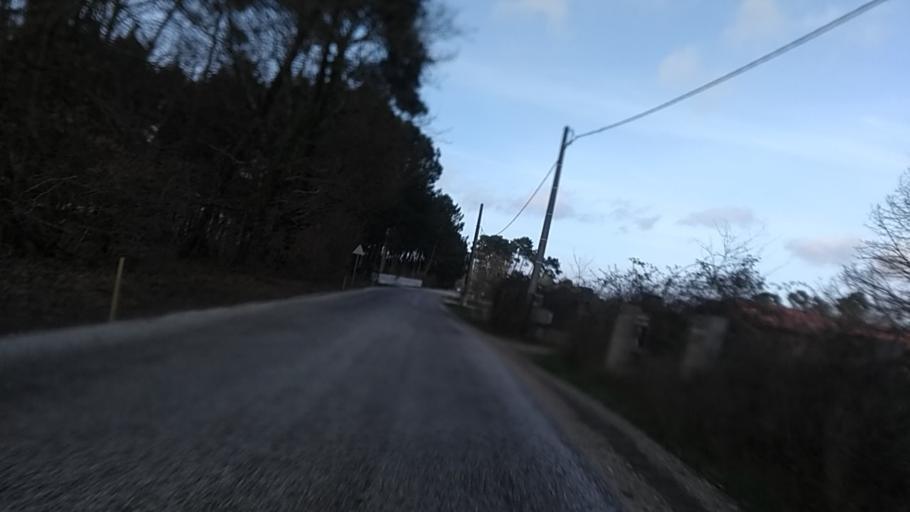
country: FR
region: Aquitaine
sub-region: Departement de la Gironde
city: Le Barp
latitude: 44.5786
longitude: -0.7709
